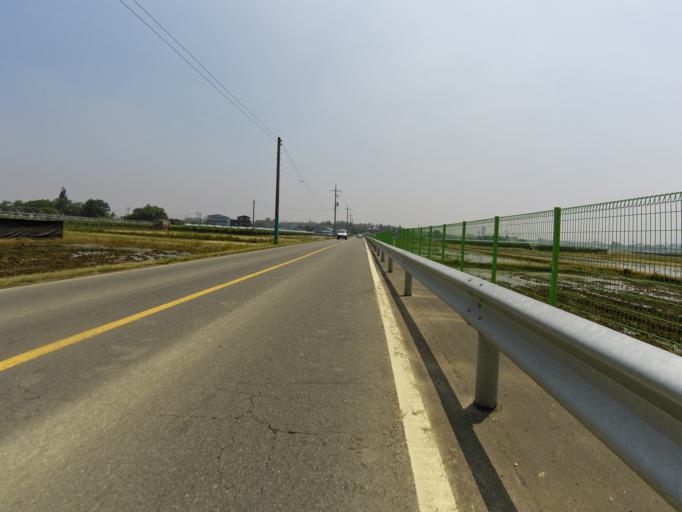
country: KR
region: Gyeongsangbuk-do
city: Gyeongsan-si
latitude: 35.8435
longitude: 128.7390
